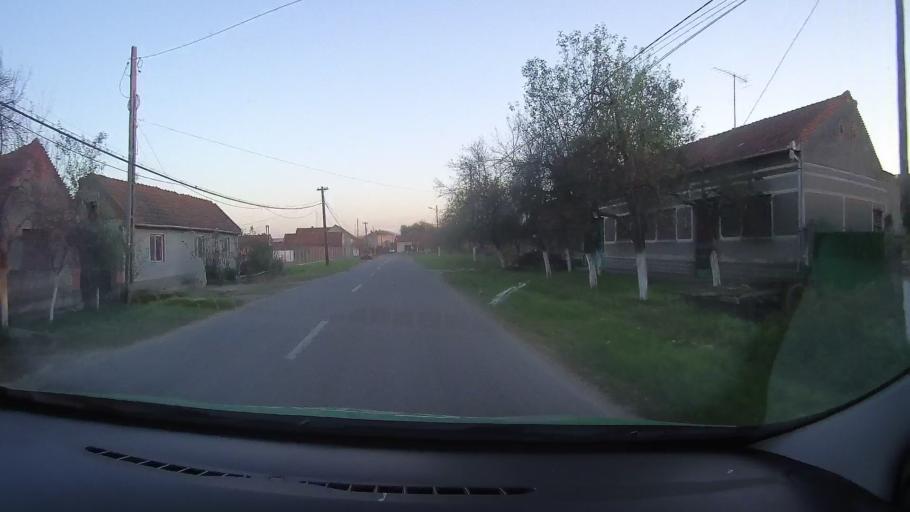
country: RO
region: Timis
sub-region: Comuna Manastiur
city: Manastiur
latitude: 45.8320
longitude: 22.0657
